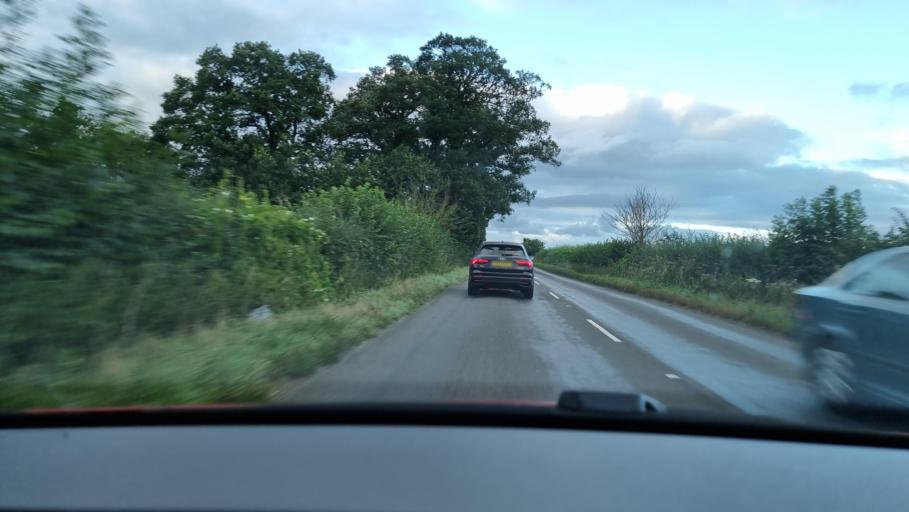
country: GB
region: England
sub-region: Milton Keynes
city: Bow Brickhill
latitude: 51.9971
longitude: -0.6976
